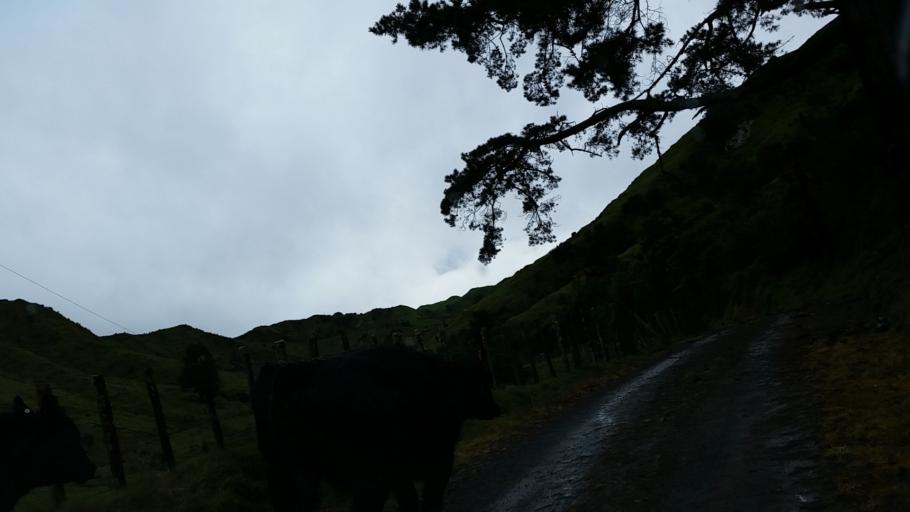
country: NZ
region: Taranaki
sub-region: South Taranaki District
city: Eltham
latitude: -39.4877
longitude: 174.4345
